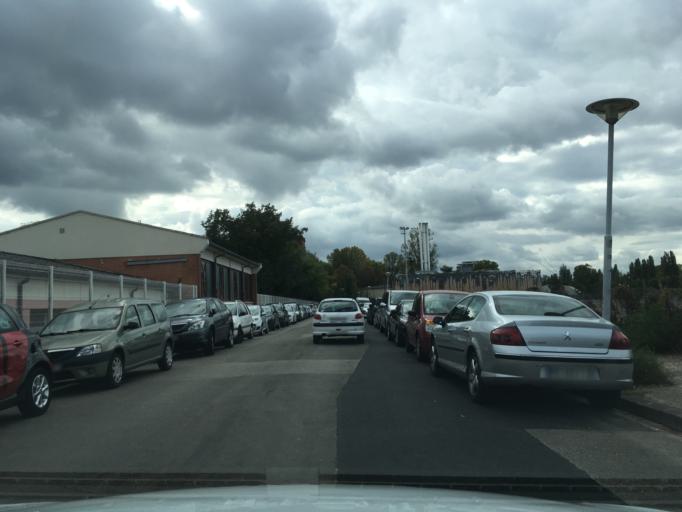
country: FR
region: Alsace
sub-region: Departement du Bas-Rhin
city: Schiltigheim
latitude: 48.5960
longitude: 7.7547
